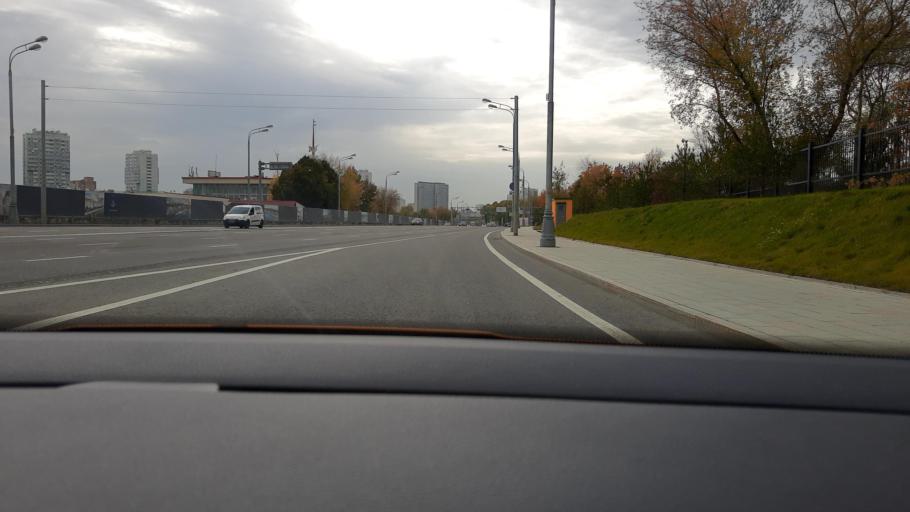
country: RU
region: Moskovskaya
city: Kozhukhovo
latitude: 55.6912
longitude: 37.6775
